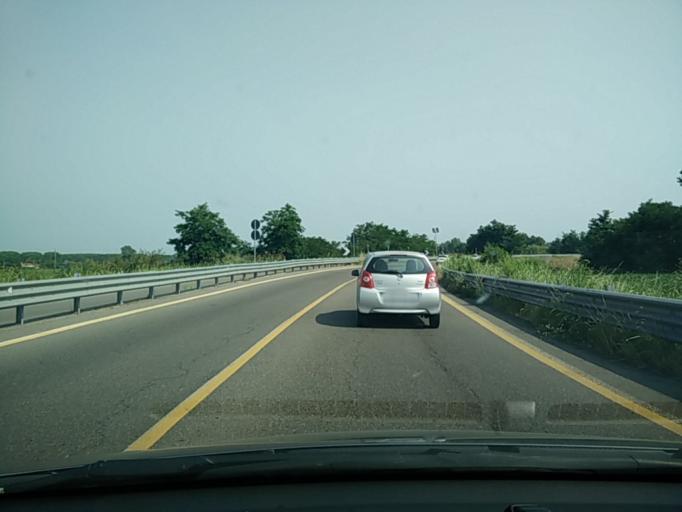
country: IT
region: Lombardy
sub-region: Provincia di Pavia
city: Valle Salimbene
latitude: 45.1500
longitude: 9.2283
